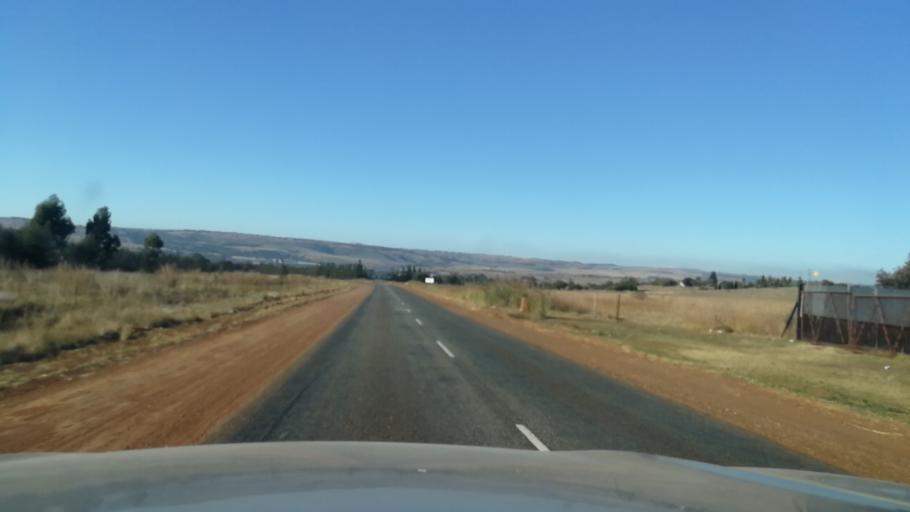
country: ZA
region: Gauteng
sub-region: West Rand District Municipality
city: Krugersdorp
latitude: -25.9989
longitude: 27.7012
